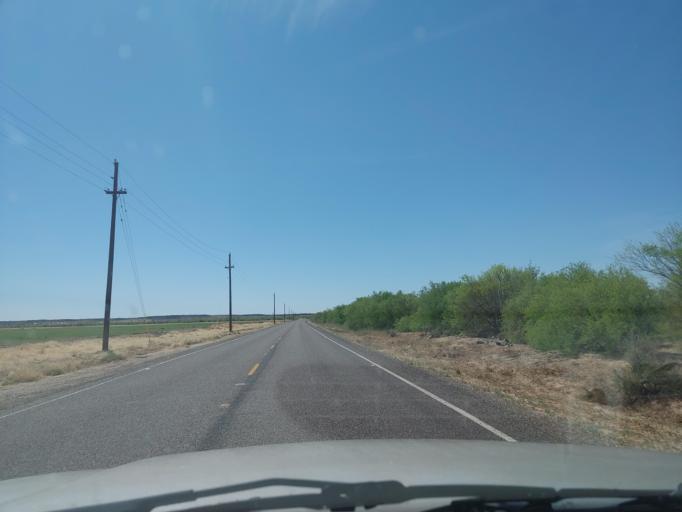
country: US
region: Arizona
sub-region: Maricopa County
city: Gila Bend
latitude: 32.9554
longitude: -113.3058
